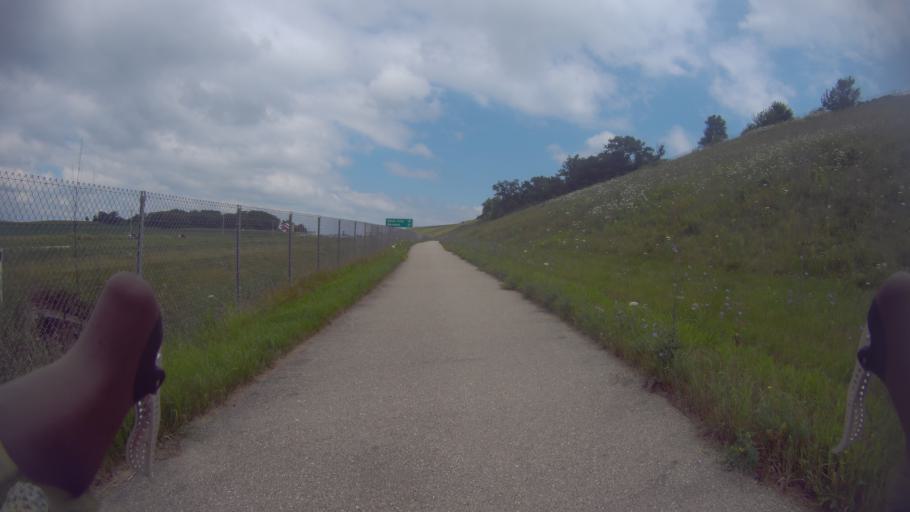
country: US
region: Wisconsin
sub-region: Dane County
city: Middleton
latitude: 43.1318
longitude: -89.5156
